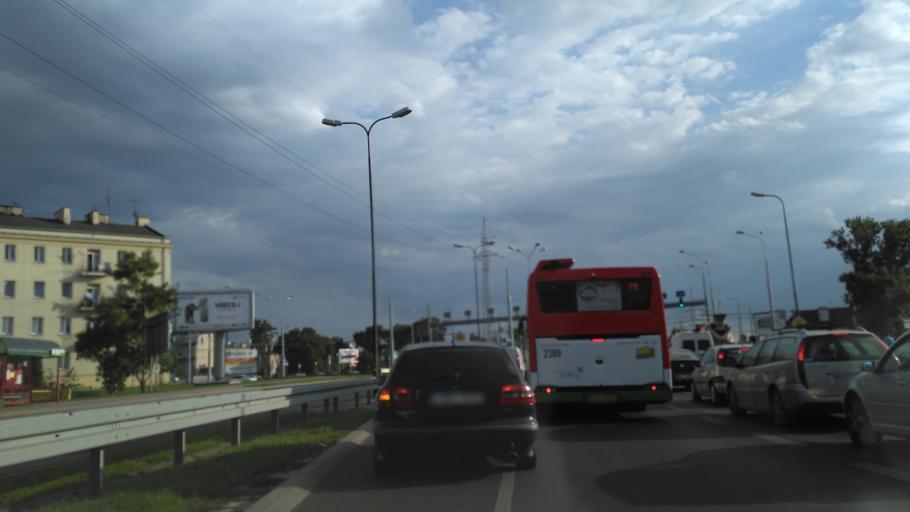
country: PL
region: Lublin Voivodeship
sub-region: Powiat lubelski
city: Lublin
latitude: 51.2358
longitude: 22.5692
